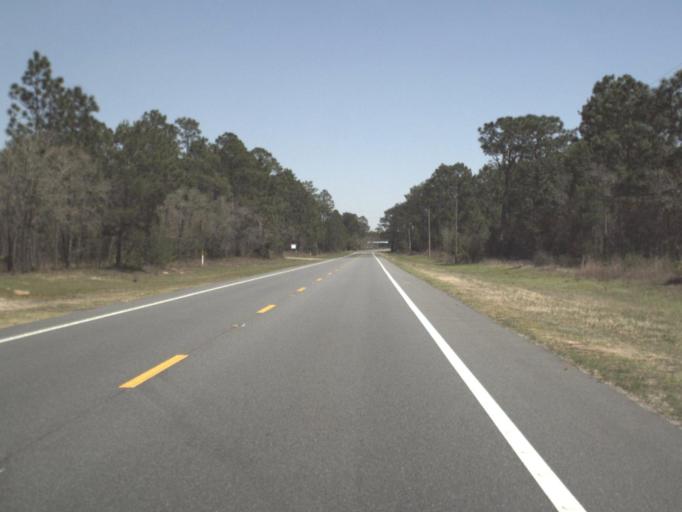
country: US
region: Florida
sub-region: Bay County
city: Youngstown
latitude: 30.4360
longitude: -85.3528
